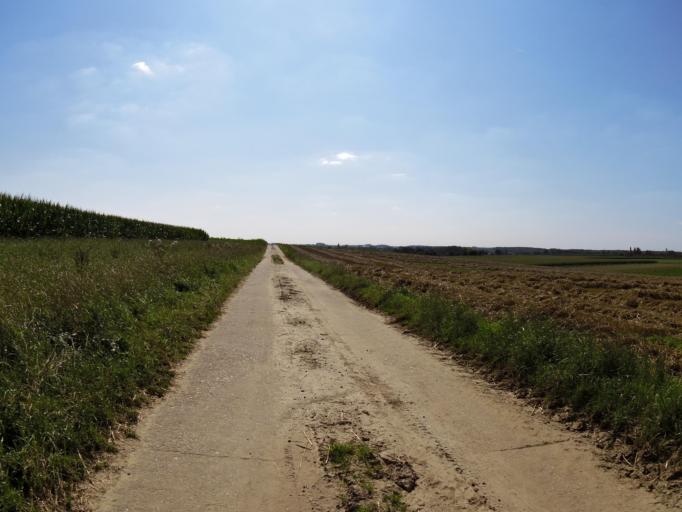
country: BE
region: Flanders
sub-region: Provincie Limburg
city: Riemst
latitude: 50.7783
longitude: 5.5421
